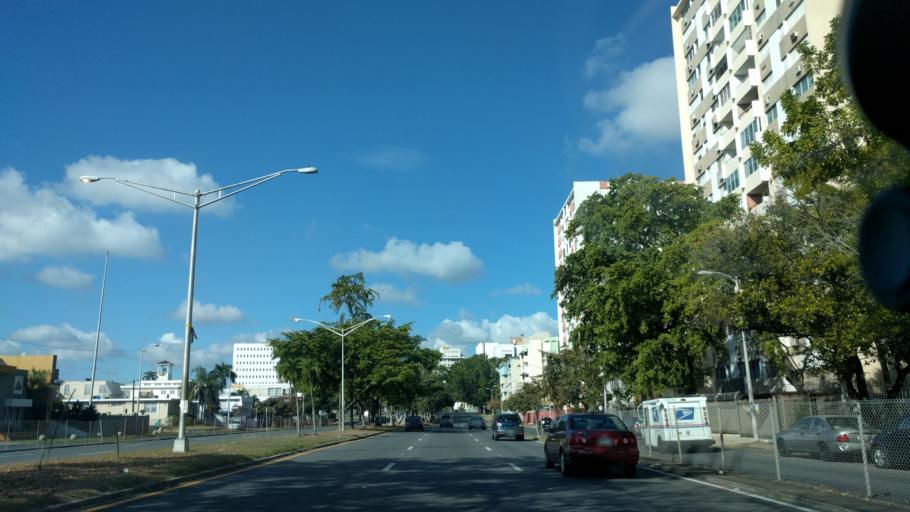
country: PR
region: San Juan
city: San Juan
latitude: 18.4251
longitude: -66.0520
